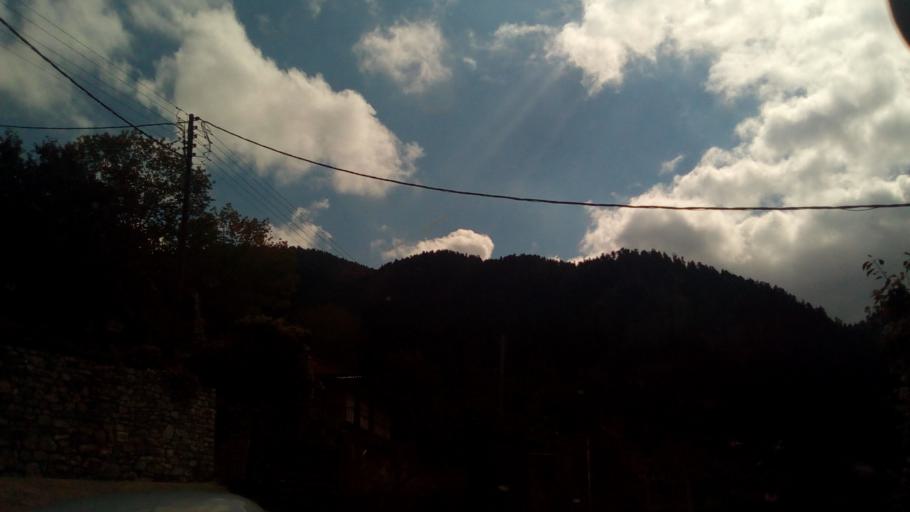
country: GR
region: West Greece
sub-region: Nomos Aitolias kai Akarnanias
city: Thermo
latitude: 38.6491
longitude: 21.9200
